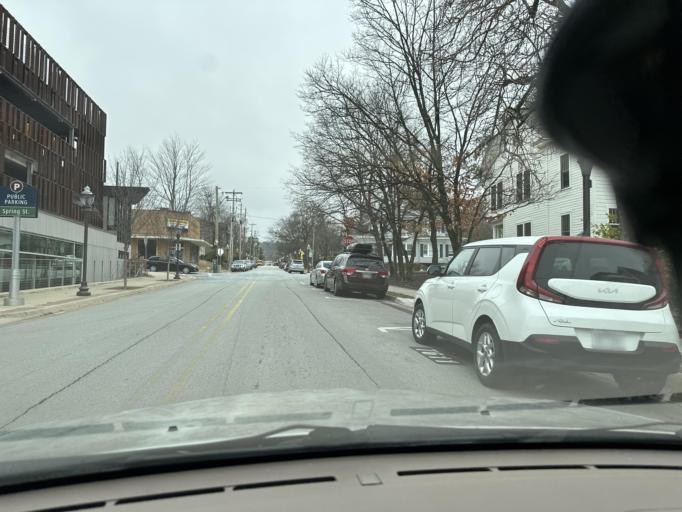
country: US
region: Arkansas
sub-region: Washington County
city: Fayetteville
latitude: 36.0647
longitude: -94.1648
